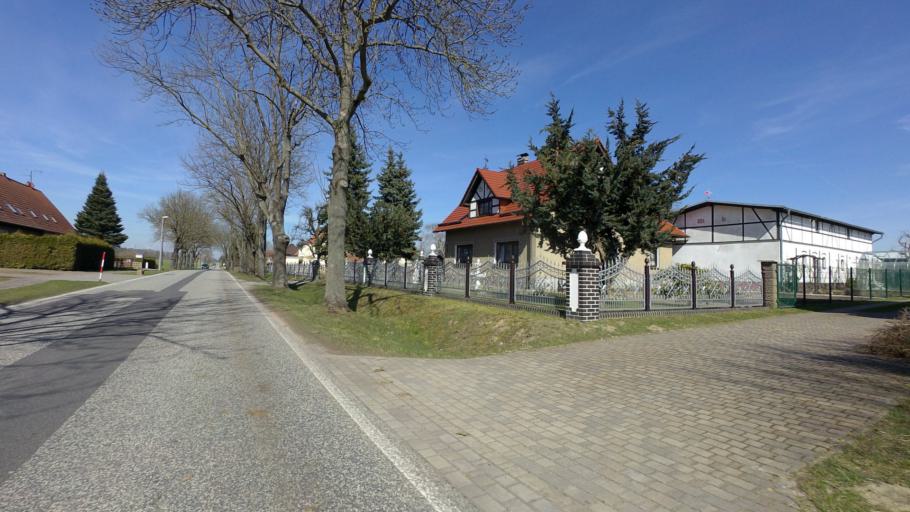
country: DE
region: Brandenburg
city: Furstenwalde
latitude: 52.4068
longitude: 14.0449
